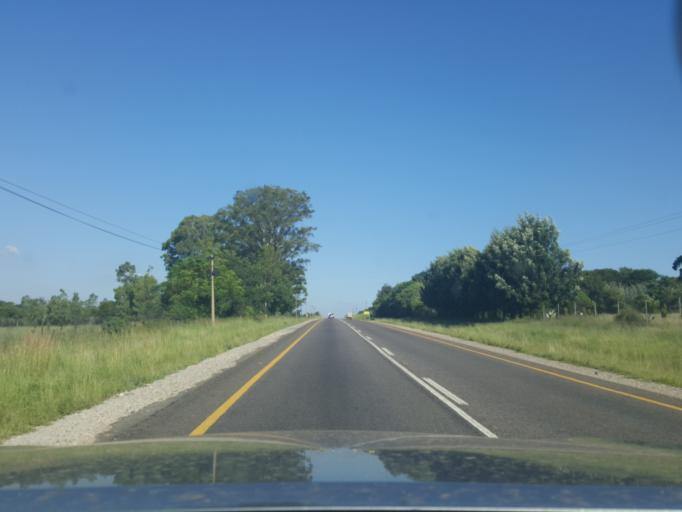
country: ZA
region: Gauteng
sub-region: City of Tshwane Metropolitan Municipality
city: Cullinan
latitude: -25.7817
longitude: 28.4984
